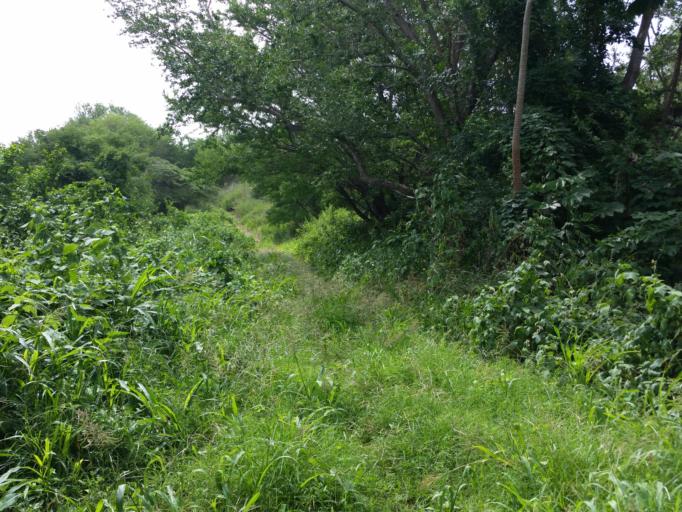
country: NI
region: Managua
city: Managua
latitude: 12.0749
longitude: -86.2505
